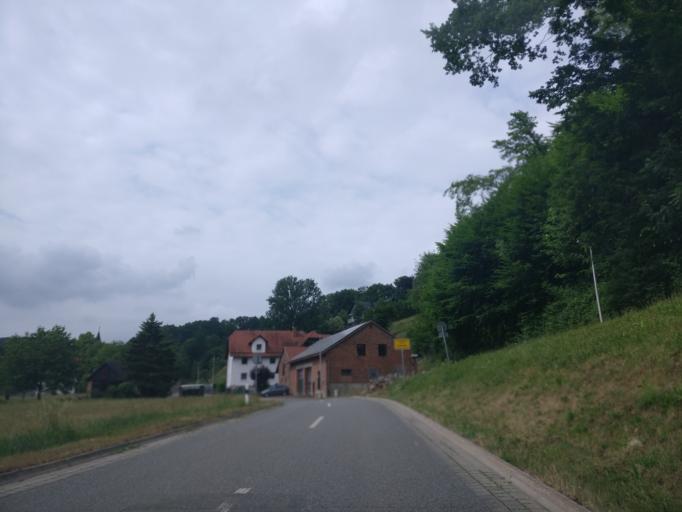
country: DE
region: Hesse
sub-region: Regierungsbezirk Kassel
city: Fuldatal
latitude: 51.3942
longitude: 9.5564
